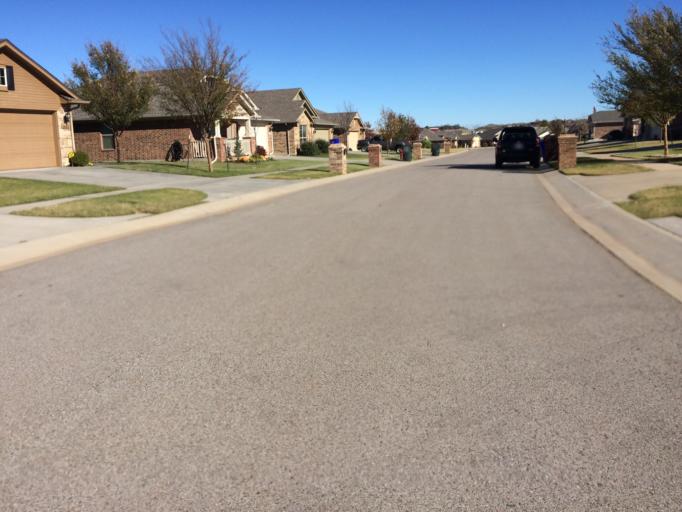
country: US
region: Oklahoma
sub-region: Cleveland County
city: Norman
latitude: 35.2612
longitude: -97.4567
